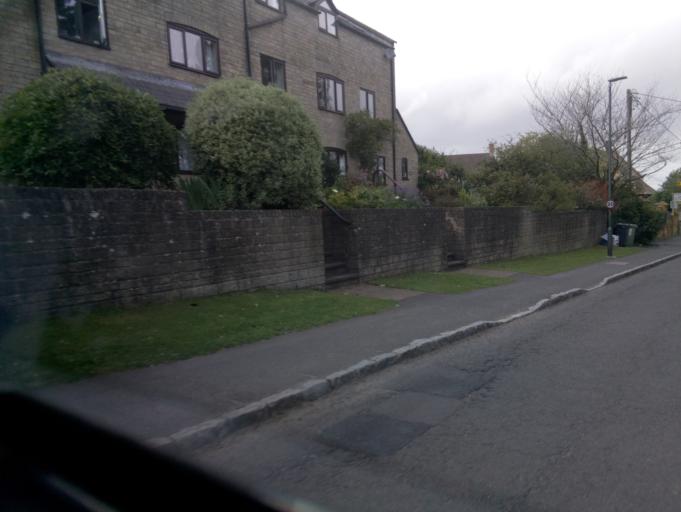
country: GB
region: England
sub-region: Gloucestershire
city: Chipping Campden
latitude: 52.0153
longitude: -1.7579
